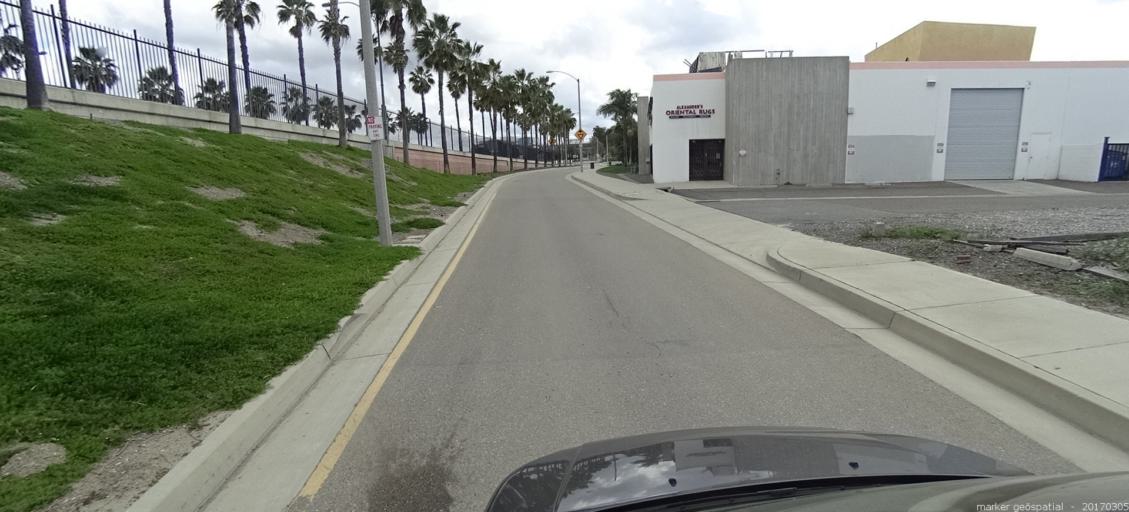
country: US
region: California
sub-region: Orange County
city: Anaheim
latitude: 33.7995
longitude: -117.8958
